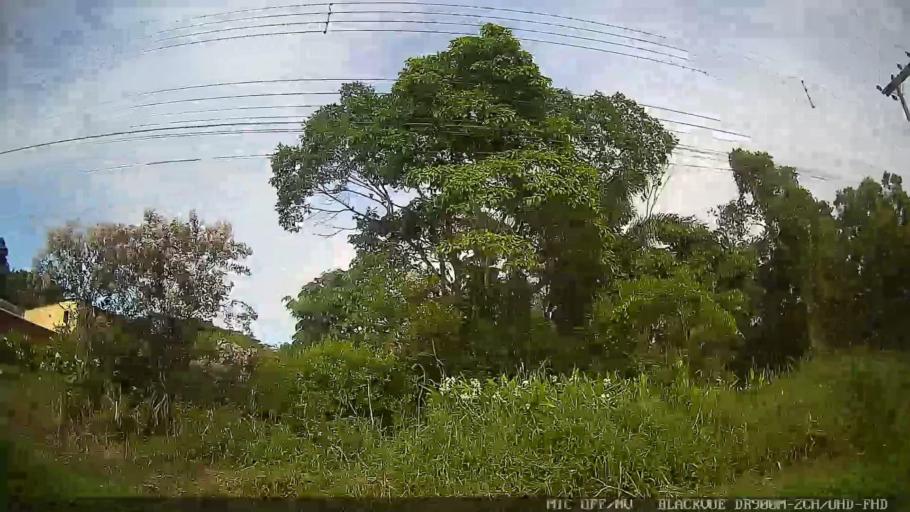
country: BR
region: Sao Paulo
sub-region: Peruibe
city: Peruibe
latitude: -24.2275
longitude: -46.9172
